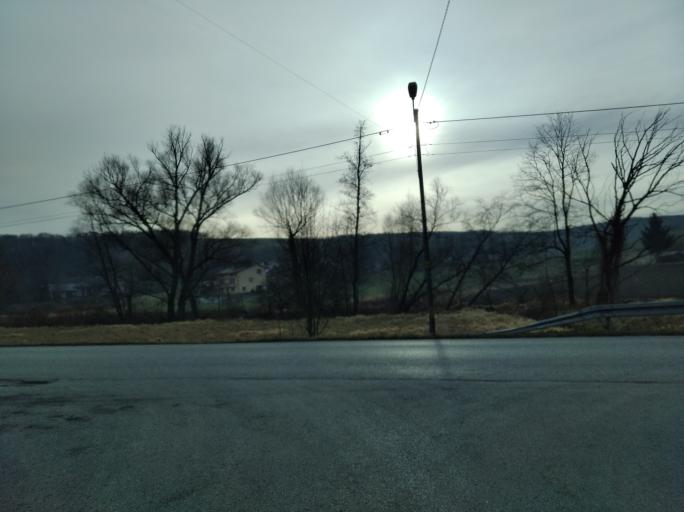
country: PL
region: Subcarpathian Voivodeship
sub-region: Powiat strzyzowski
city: Czudec
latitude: 49.9247
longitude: 21.8002
